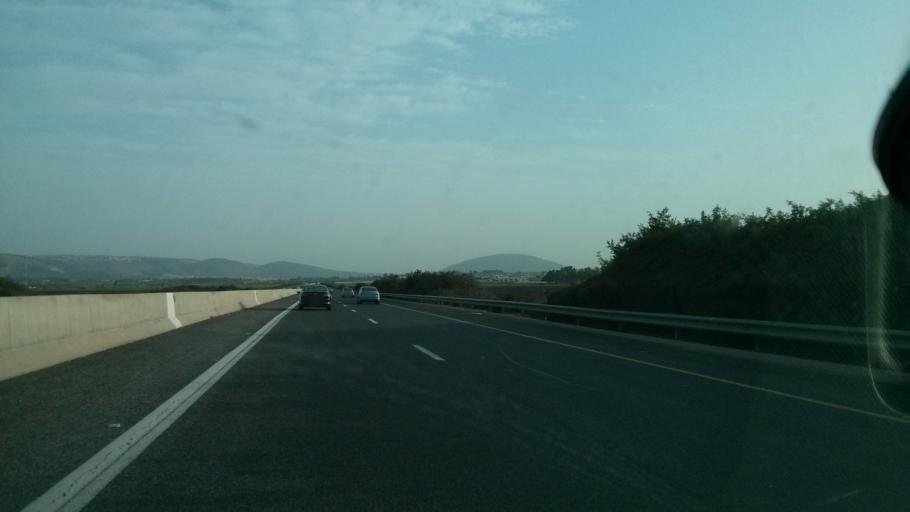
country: IL
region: Northern District
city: `Afula `Illit
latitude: 32.6065
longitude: 35.2661
